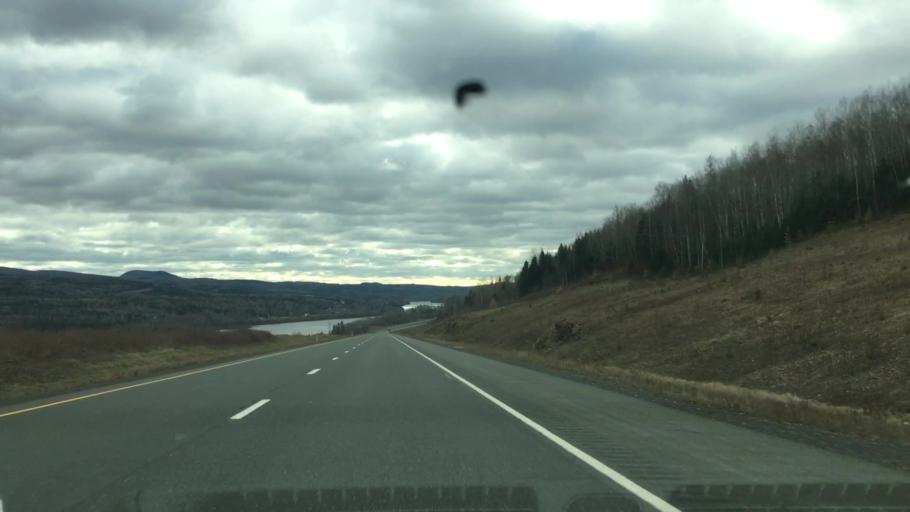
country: US
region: Maine
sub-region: Aroostook County
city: Fort Fairfield
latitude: 46.6884
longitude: -67.7366
